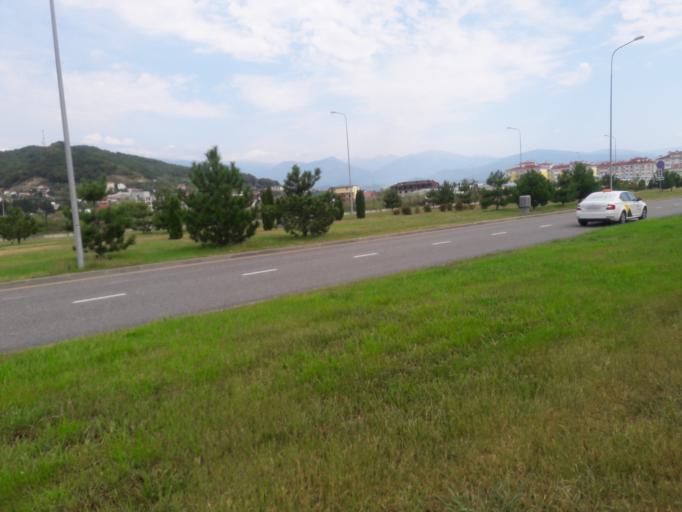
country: RU
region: Krasnodarskiy
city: Adler
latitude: 43.4042
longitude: 39.9779
